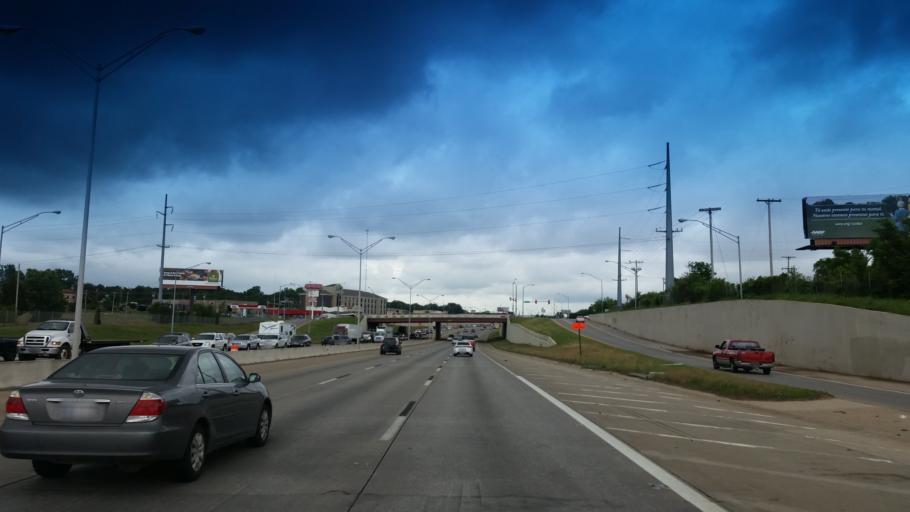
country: US
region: Oklahoma
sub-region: Oklahoma County
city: Oklahoma City
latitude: 35.4521
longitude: -97.4887
